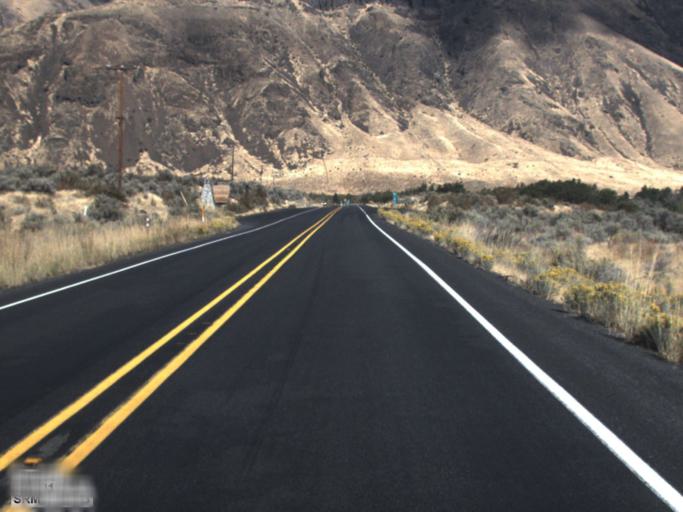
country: US
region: Washington
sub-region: Yakima County
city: Tieton
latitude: 46.7404
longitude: -120.7894
